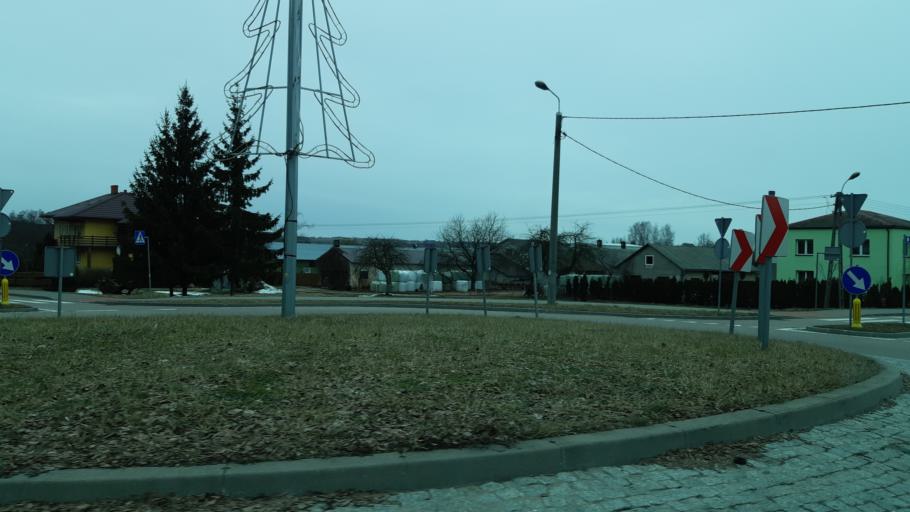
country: PL
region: Podlasie
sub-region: Suwalki
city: Suwalki
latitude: 54.3225
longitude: 22.9724
